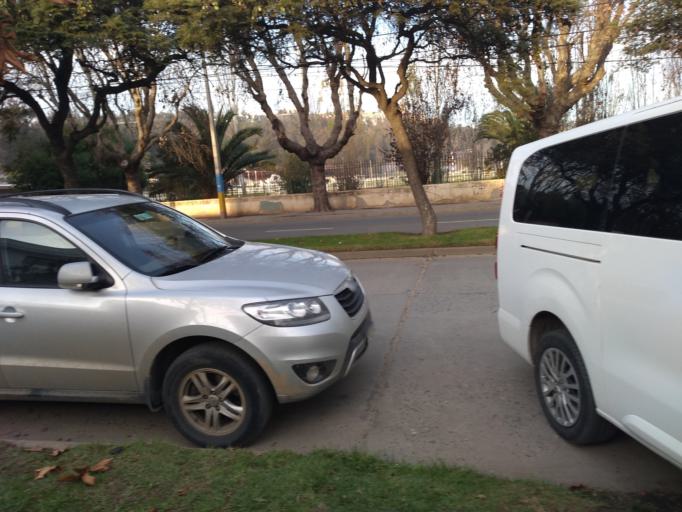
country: CL
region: Valparaiso
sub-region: Provincia de Valparaiso
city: Vina del Mar
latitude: -33.0210
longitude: -71.5415
